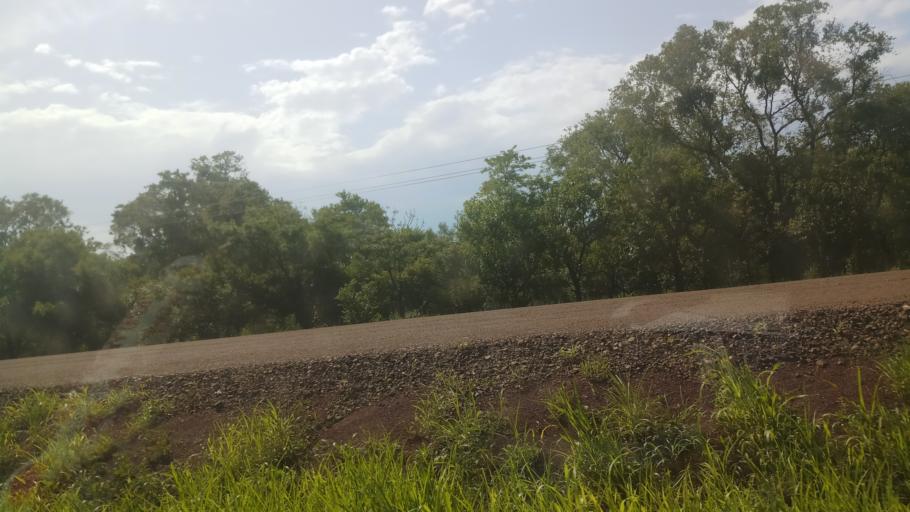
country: ET
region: Gambela
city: Gambela
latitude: 8.1538
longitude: 34.4500
